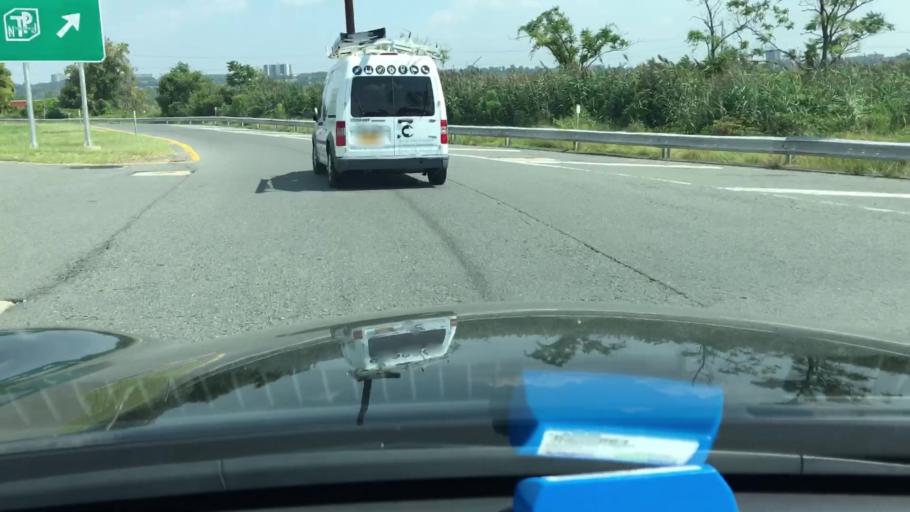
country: US
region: New Jersey
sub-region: Bergen County
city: Moonachie
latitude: 40.8216
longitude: -74.0300
